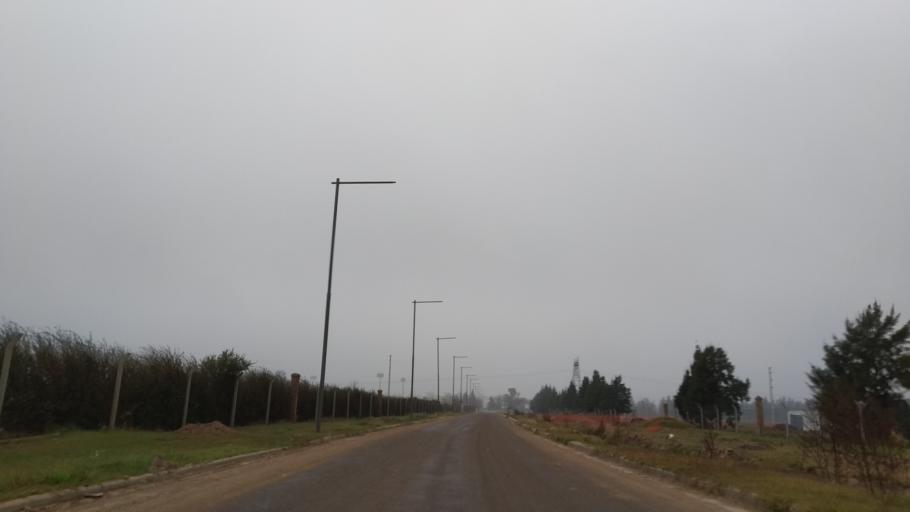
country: AR
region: Santa Fe
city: Funes
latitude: -32.9413
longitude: -60.7676
